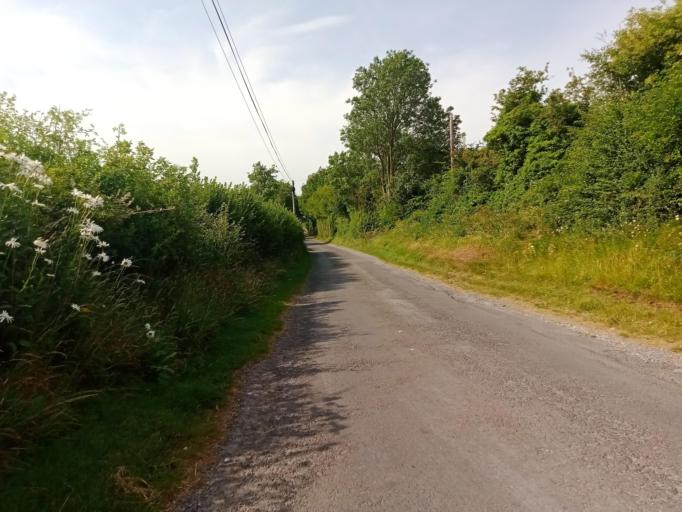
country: IE
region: Leinster
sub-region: Laois
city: Rathdowney
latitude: 52.8144
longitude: -7.4715
